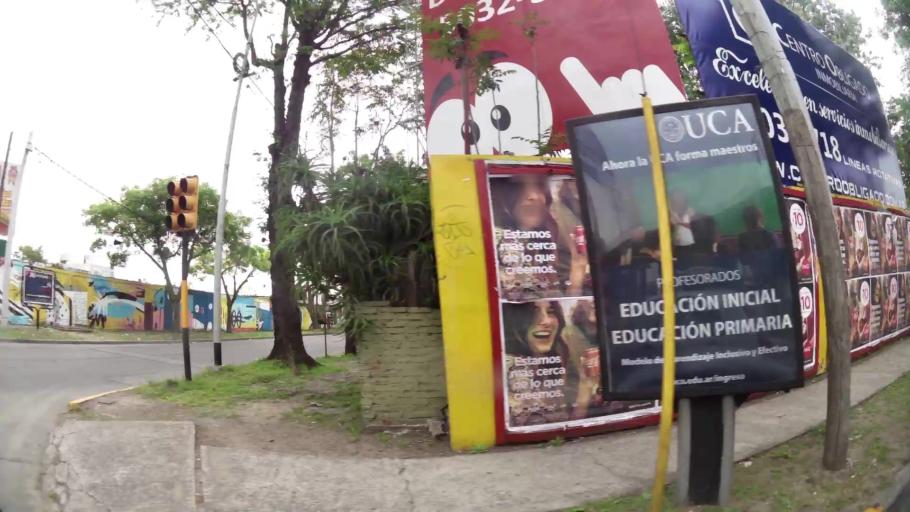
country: AR
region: Buenos Aires
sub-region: Partido de Avellaneda
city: Avellaneda
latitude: -34.6733
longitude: -58.3602
